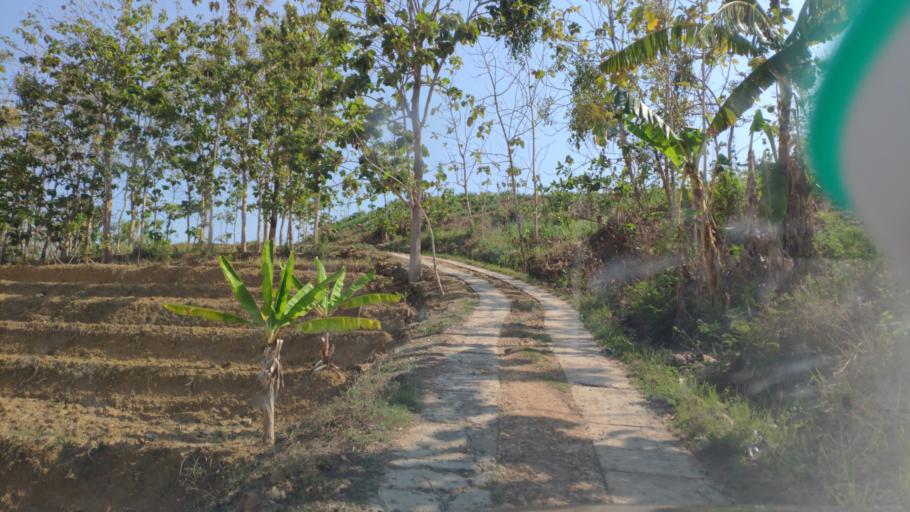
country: ID
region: Central Java
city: Ngapus
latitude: -6.9367
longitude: 111.2123
